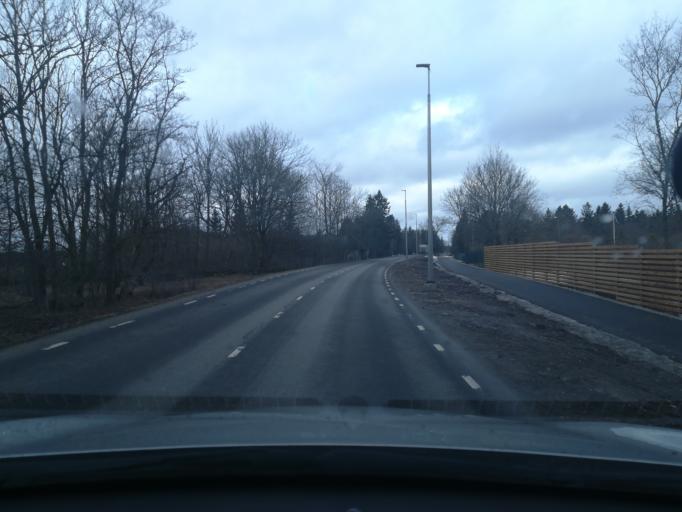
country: EE
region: Harju
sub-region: Harku vald
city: Tabasalu
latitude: 59.4253
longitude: 24.5300
